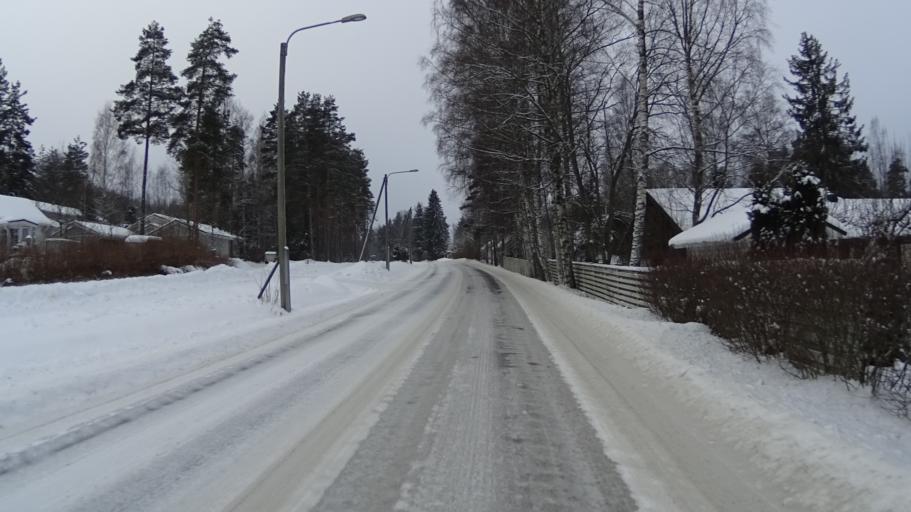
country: FI
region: Uusimaa
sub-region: Helsinki
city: Vihti
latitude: 60.3386
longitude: 24.2924
